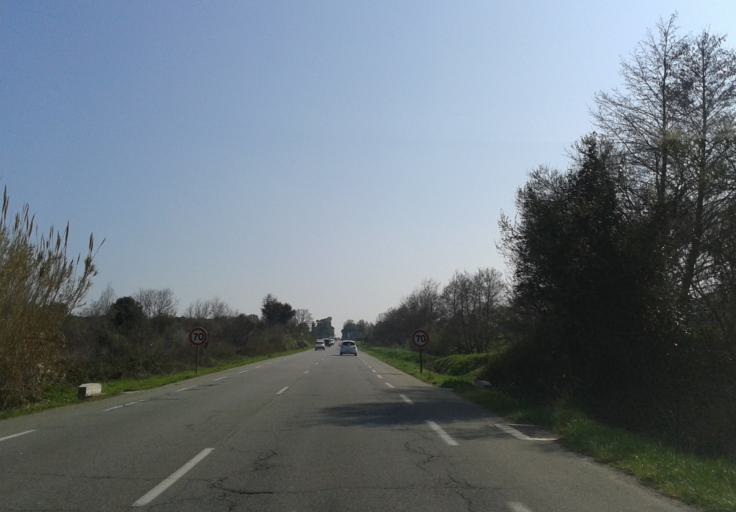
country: FR
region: Corsica
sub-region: Departement de la Haute-Corse
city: San-Nicolao
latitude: 42.3464
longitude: 9.5335
